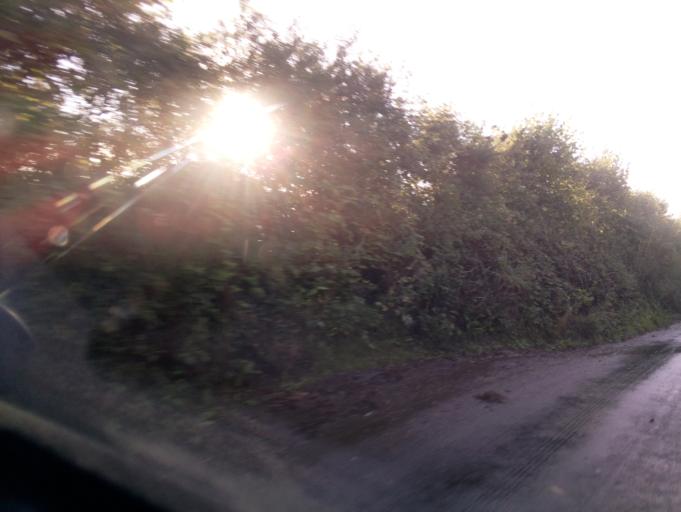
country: GB
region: England
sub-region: Devon
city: Totnes
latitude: 50.3507
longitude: -3.7171
